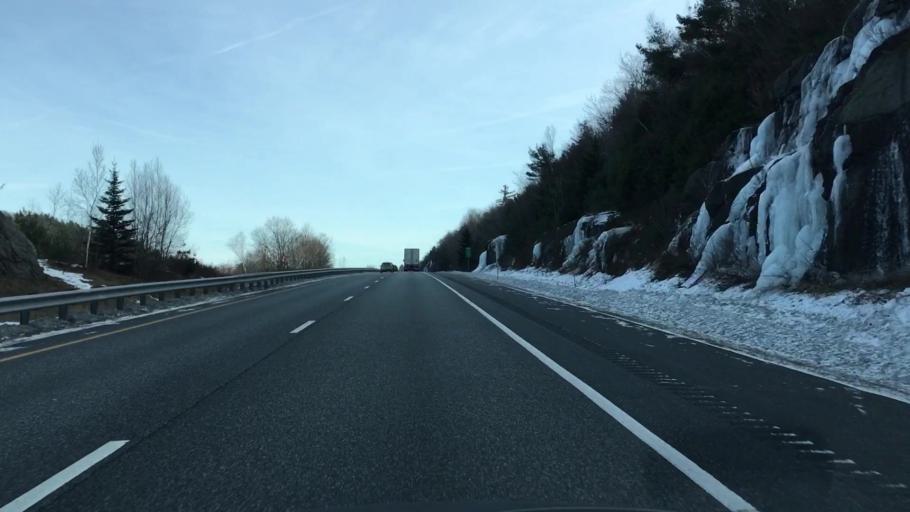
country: US
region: New Hampshire
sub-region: Sullivan County
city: Sunapee
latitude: 43.4497
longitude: -72.0861
